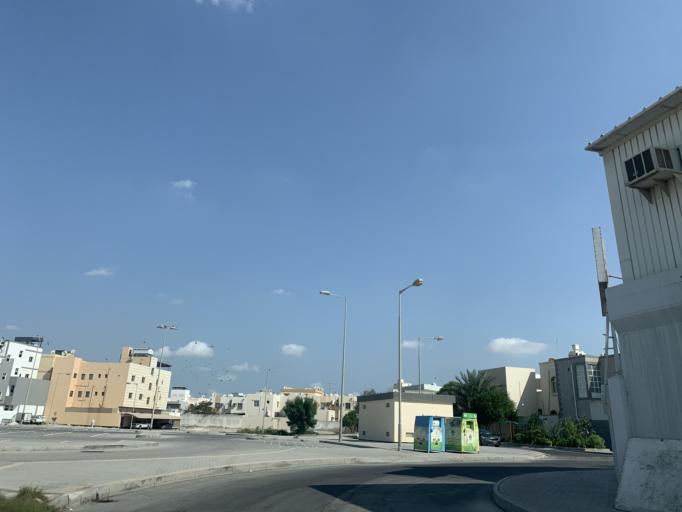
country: BH
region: Central Governorate
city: Madinat Hamad
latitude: 26.1370
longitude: 50.4986
